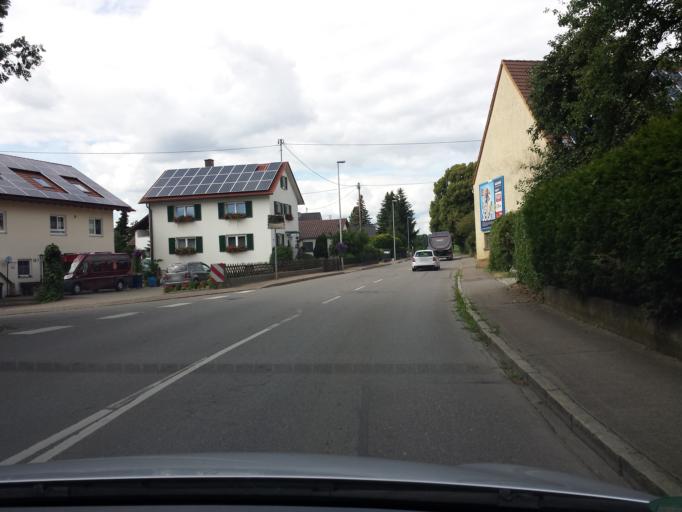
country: DE
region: Baden-Wuerttemberg
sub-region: Tuebingen Region
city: Schwendi
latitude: 48.2109
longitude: 9.9594
